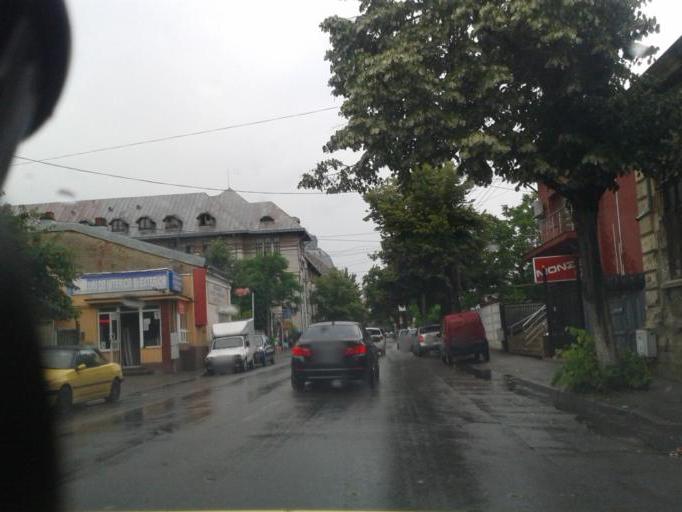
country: RO
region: Prahova
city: Ploiesti
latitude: 44.9456
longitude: 26.0278
